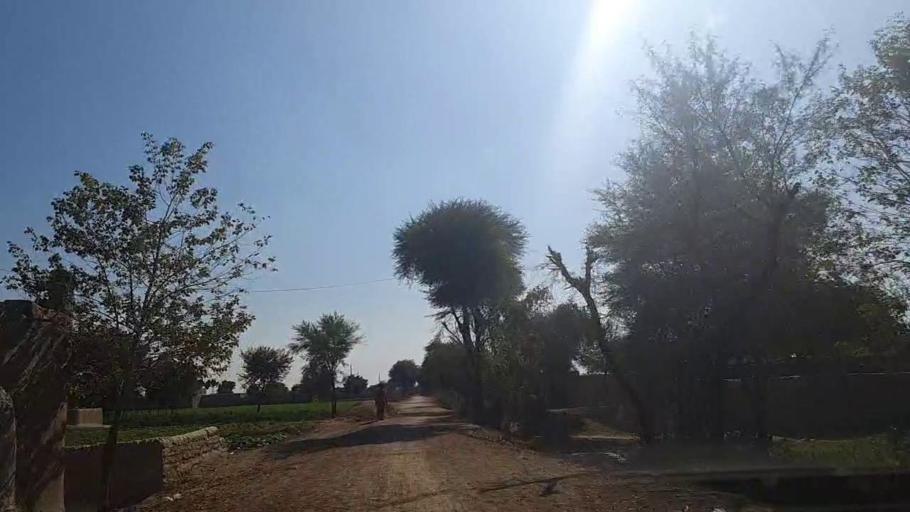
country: PK
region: Sindh
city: Sakrand
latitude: 26.2351
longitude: 68.1998
